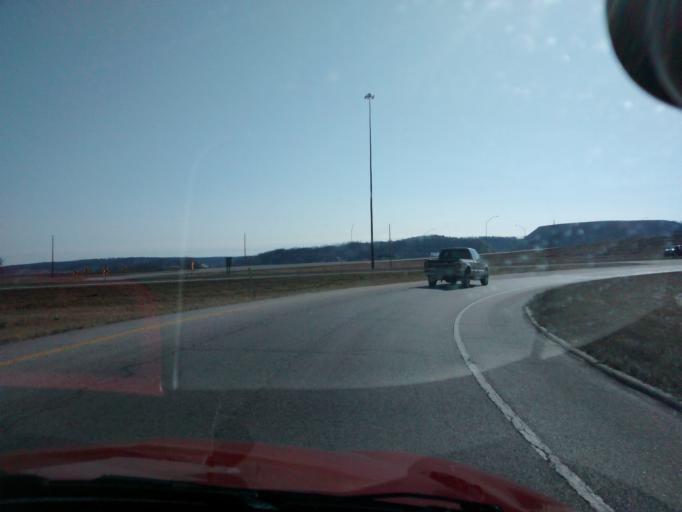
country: US
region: Iowa
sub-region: Pottawattamie County
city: Carter Lake
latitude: 41.3556
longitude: -95.9020
